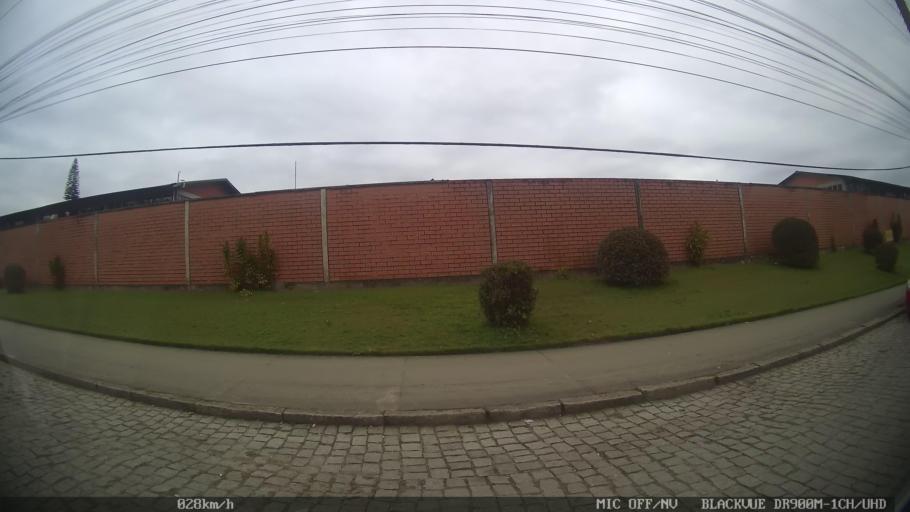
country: BR
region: Santa Catarina
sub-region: Joinville
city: Joinville
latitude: -26.2582
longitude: -48.8727
